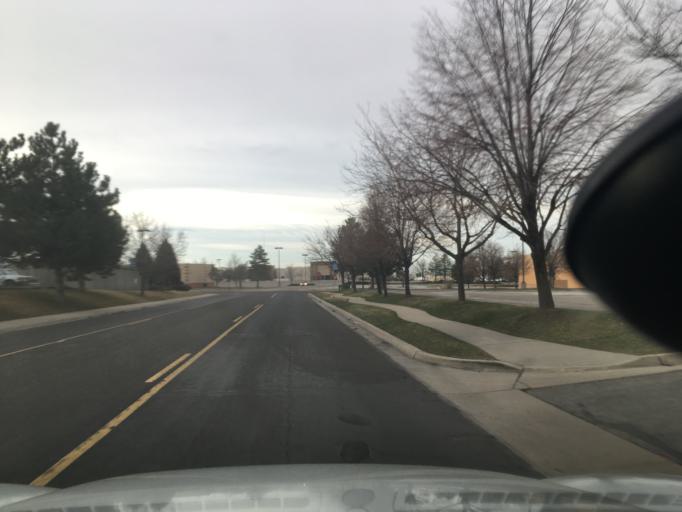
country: US
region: Utah
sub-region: Davis County
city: Layton
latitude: 41.0815
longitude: -111.9784
